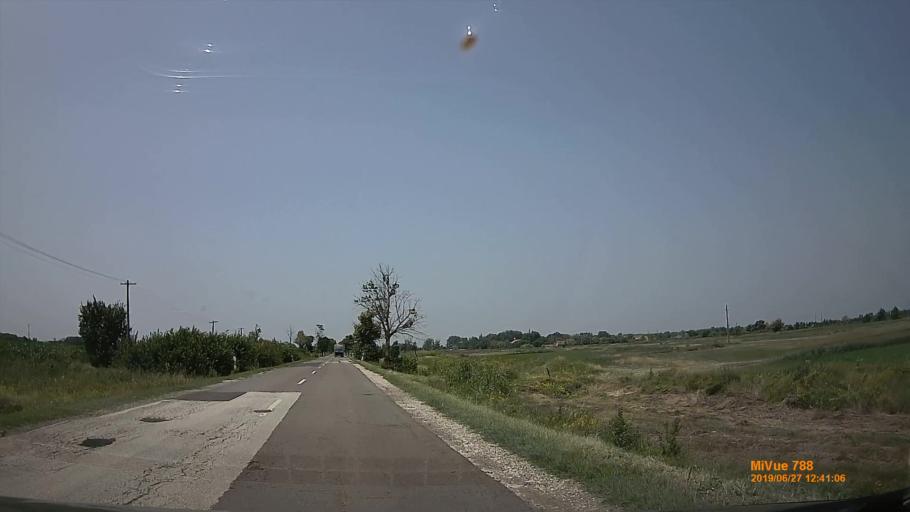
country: HU
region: Pest
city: Tortel
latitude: 47.1794
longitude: 19.9016
